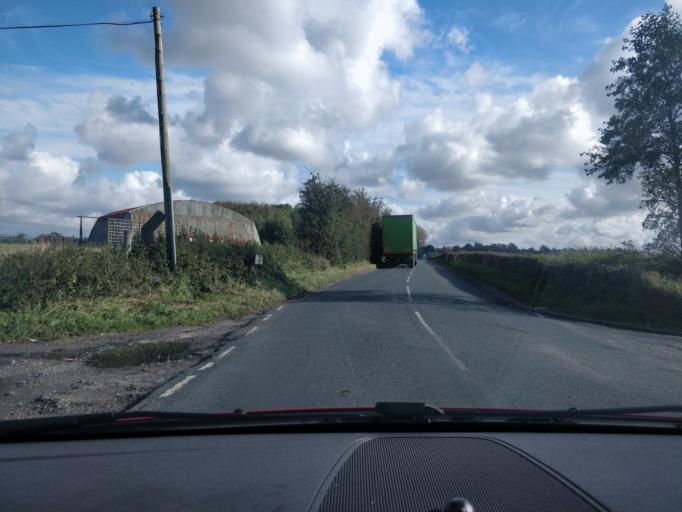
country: GB
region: England
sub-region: Lancashire
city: Ormskirk
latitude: 53.5897
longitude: -2.8767
